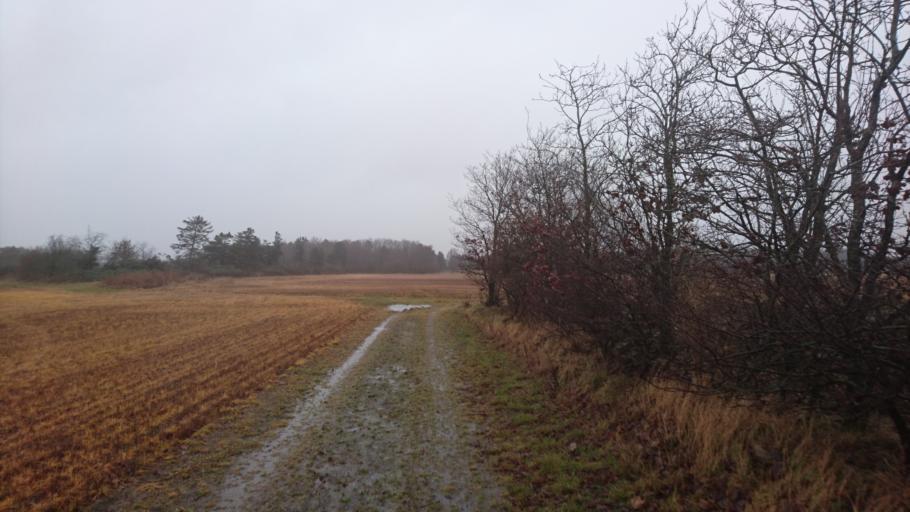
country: DK
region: Central Jutland
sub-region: Herning Kommune
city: Sunds
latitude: 56.1941
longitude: 9.0283
